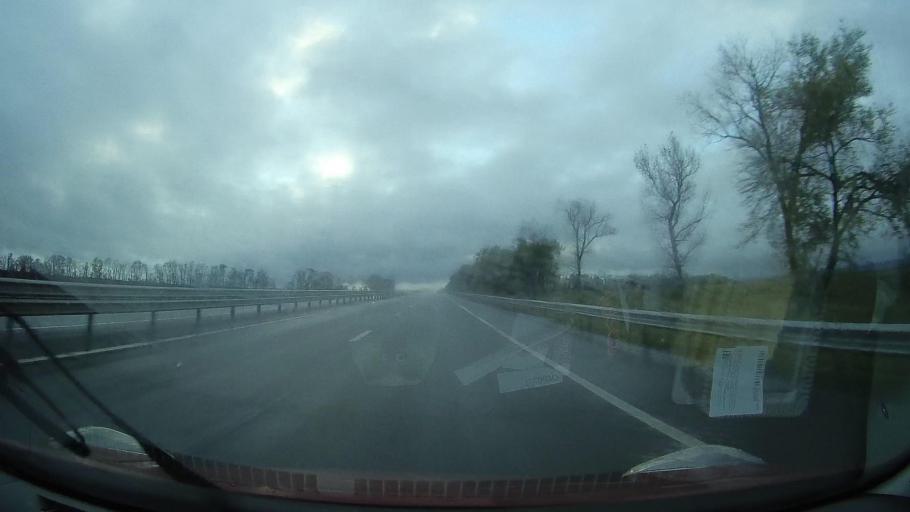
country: RU
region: Stavropol'skiy
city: Zavetnoye
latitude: 44.7869
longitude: 41.5120
